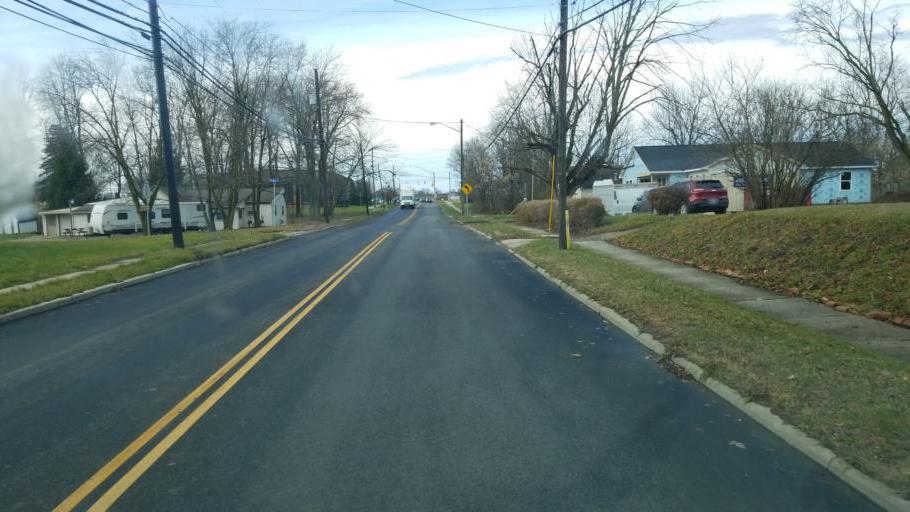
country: US
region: Ohio
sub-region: Delaware County
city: Delaware
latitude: 40.2907
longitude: -83.0769
